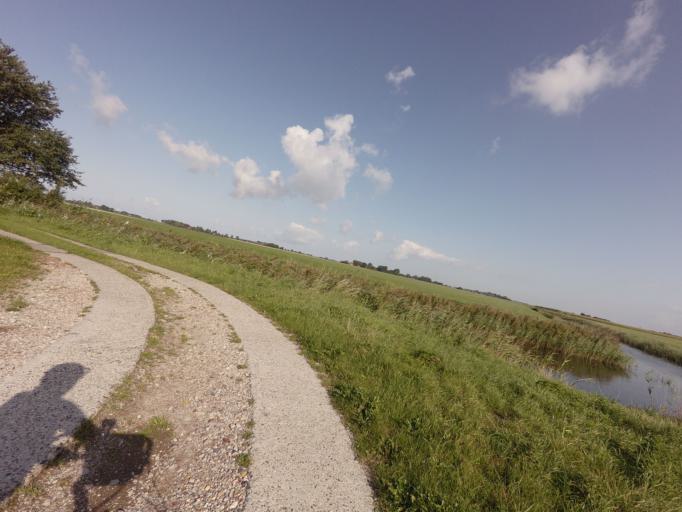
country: NL
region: Friesland
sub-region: Gemeente Franekeradeel
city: Franeker
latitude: 53.2038
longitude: 5.5715
